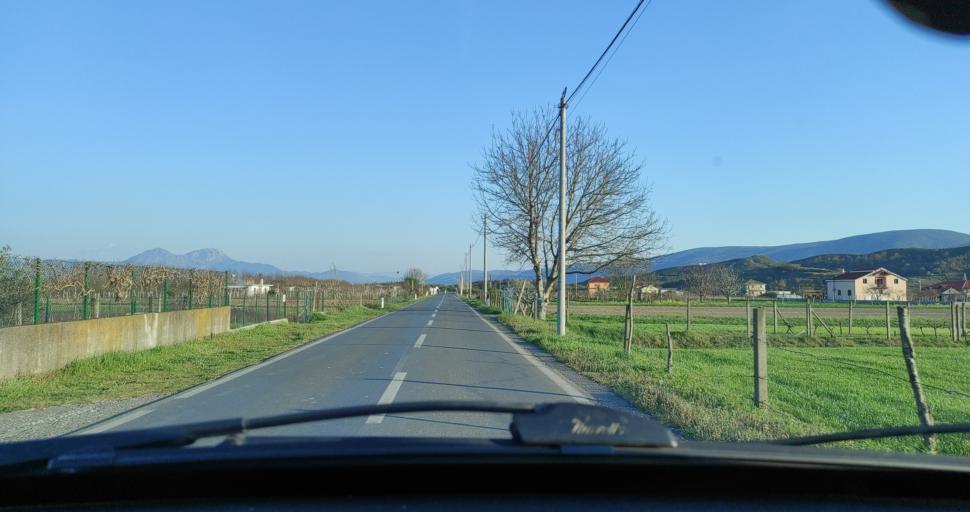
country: AL
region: Lezhe
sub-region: Rrethi i Lezhes
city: Dajc
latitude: 41.9476
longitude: 19.5324
